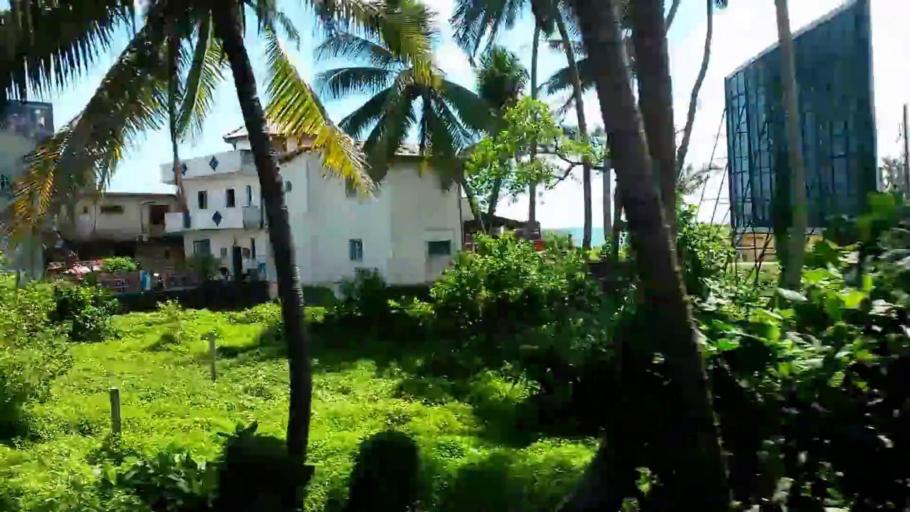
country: LK
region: Southern
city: Hikkaduwa
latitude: 6.1607
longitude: 80.0937
